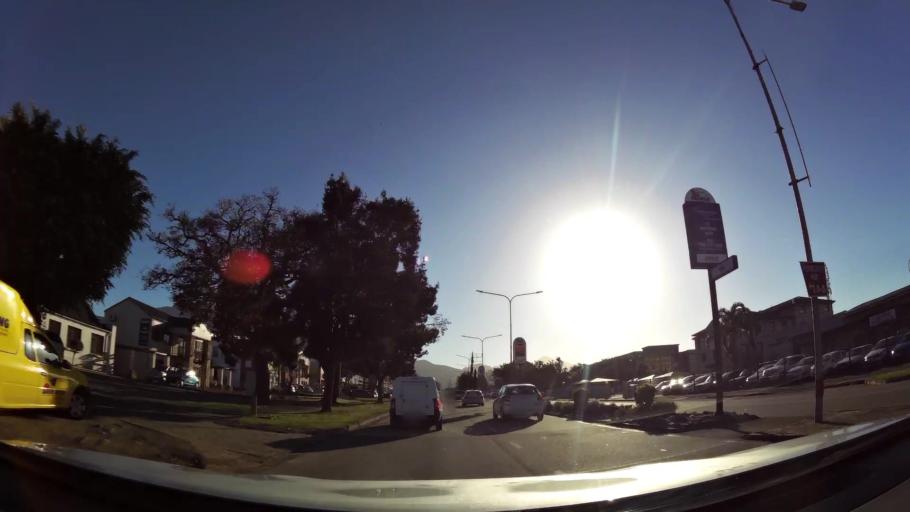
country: ZA
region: Western Cape
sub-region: Eden District Municipality
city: George
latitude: -33.9651
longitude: 22.4517
